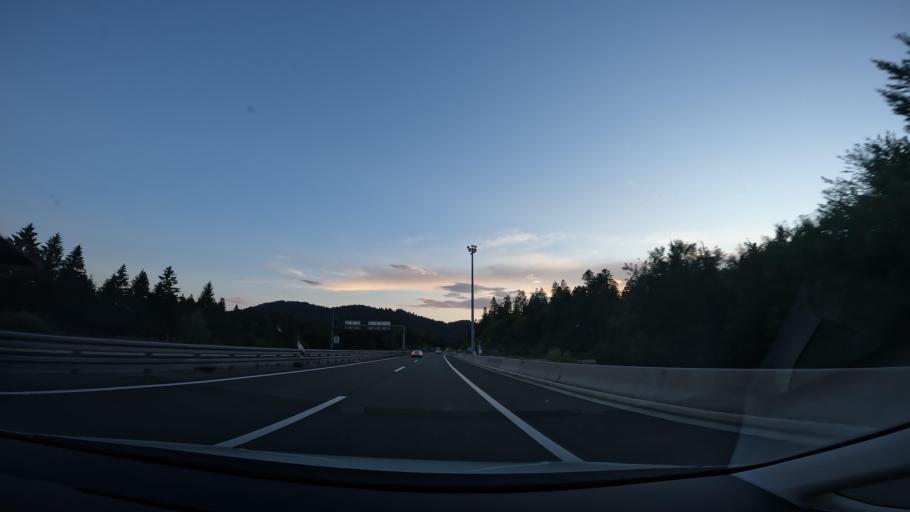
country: HR
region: Primorsko-Goranska
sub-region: Grad Delnice
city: Delnice
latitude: 45.3752
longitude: 14.7922
